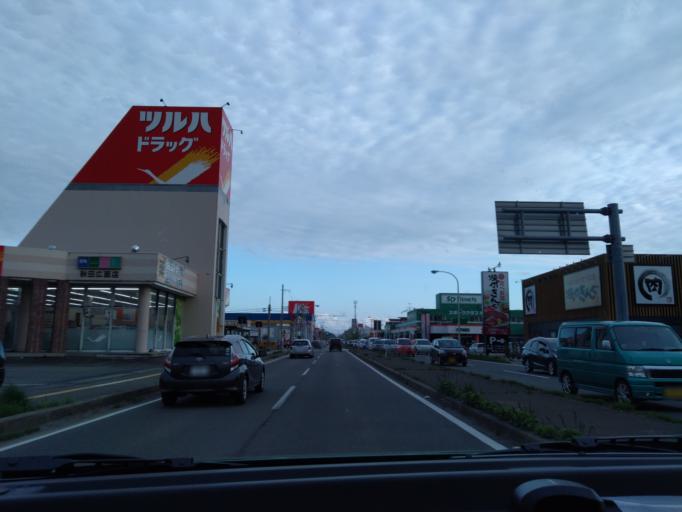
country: JP
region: Akita
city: Akita
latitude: 39.7171
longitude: 140.1486
